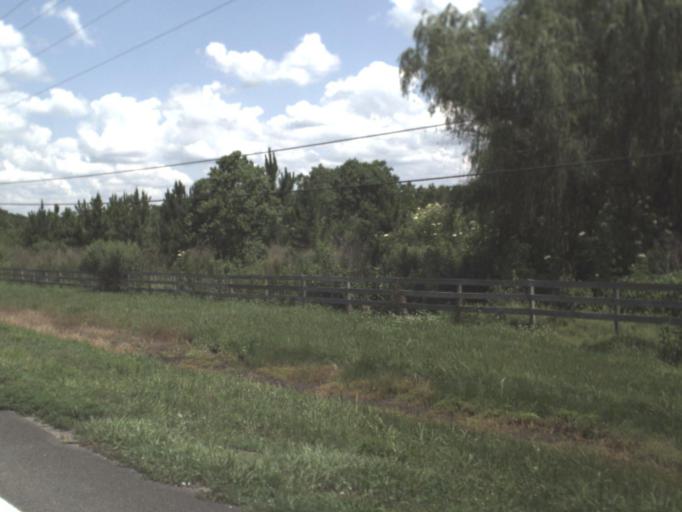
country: US
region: Florida
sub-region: Nassau County
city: Nassau Village-Ratliff
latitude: 30.5113
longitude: -81.7580
